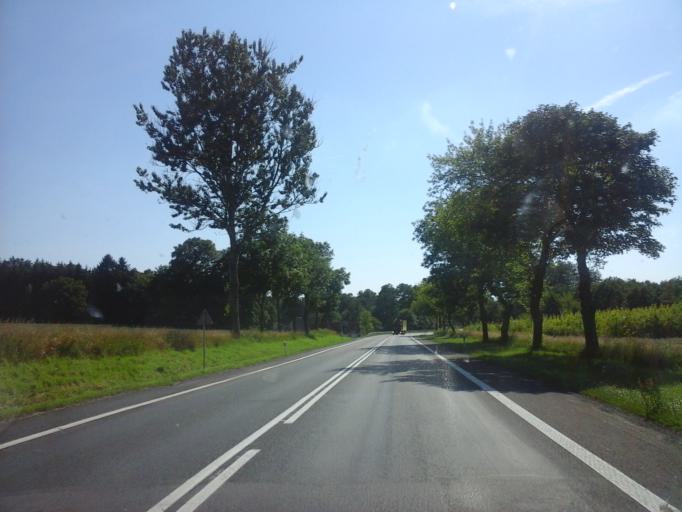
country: PL
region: West Pomeranian Voivodeship
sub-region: Powiat bialogardzki
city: Karlino
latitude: 53.9972
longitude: 15.7738
